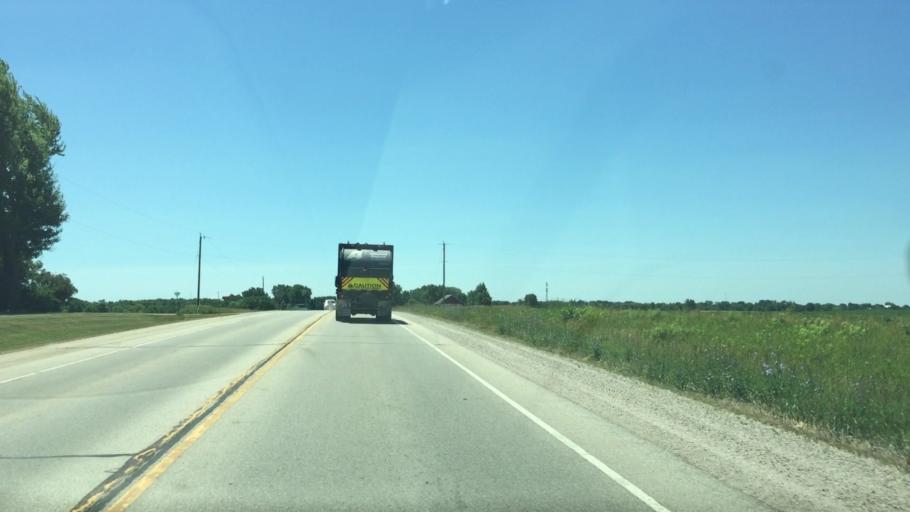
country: US
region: Wisconsin
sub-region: Calumet County
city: Chilton
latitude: 44.0569
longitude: -88.1631
